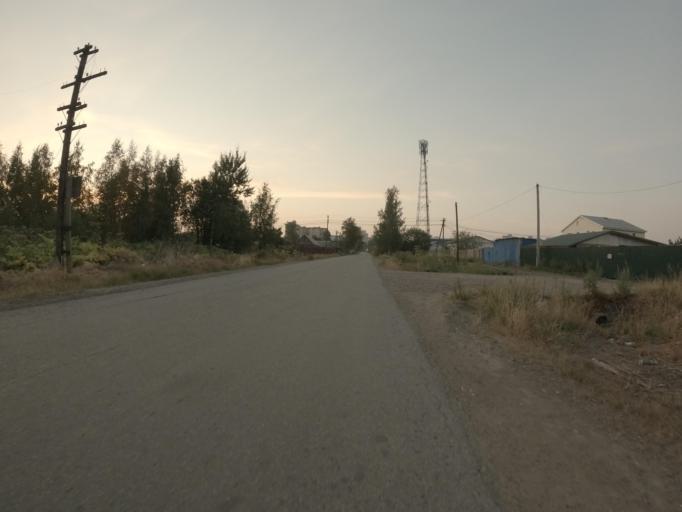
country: RU
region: Leningrad
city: Yanino Vtoroye
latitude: 59.9442
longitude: 30.5543
